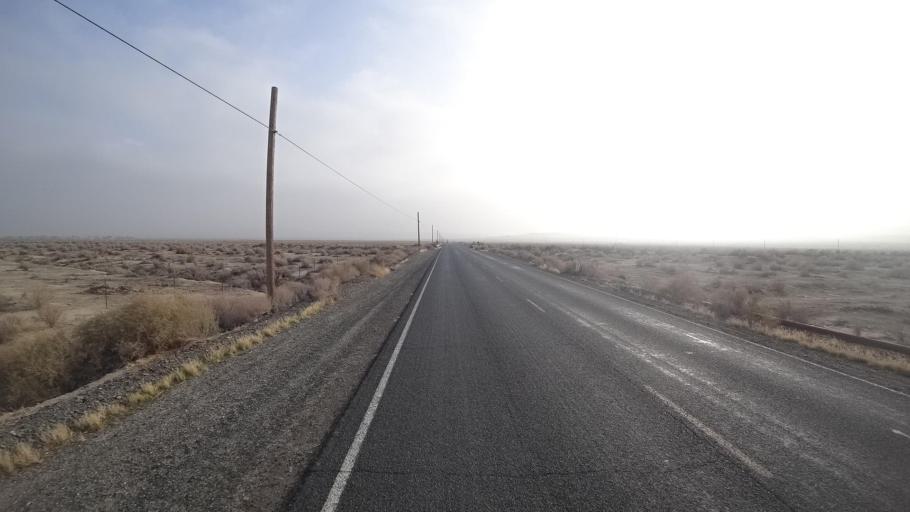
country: US
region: California
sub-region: Kern County
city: Ford City
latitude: 35.2236
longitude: -119.4456
